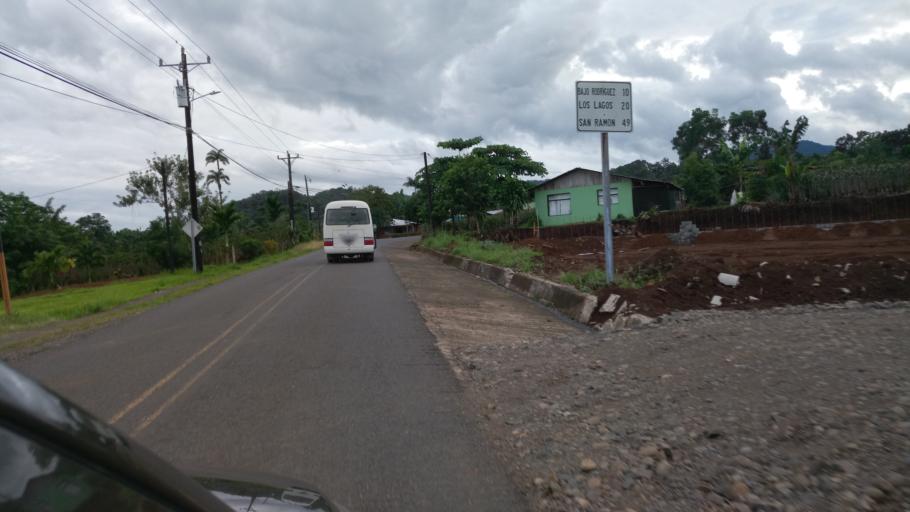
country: CR
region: Alajuela
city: Pocosol
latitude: 10.3386
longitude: -84.5812
